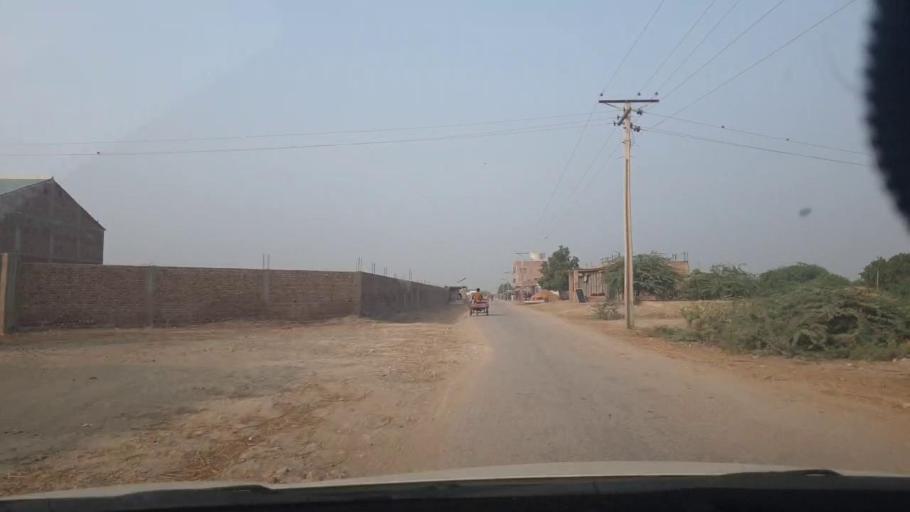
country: PK
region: Sindh
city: Bulri
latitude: 24.7576
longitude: 68.4193
